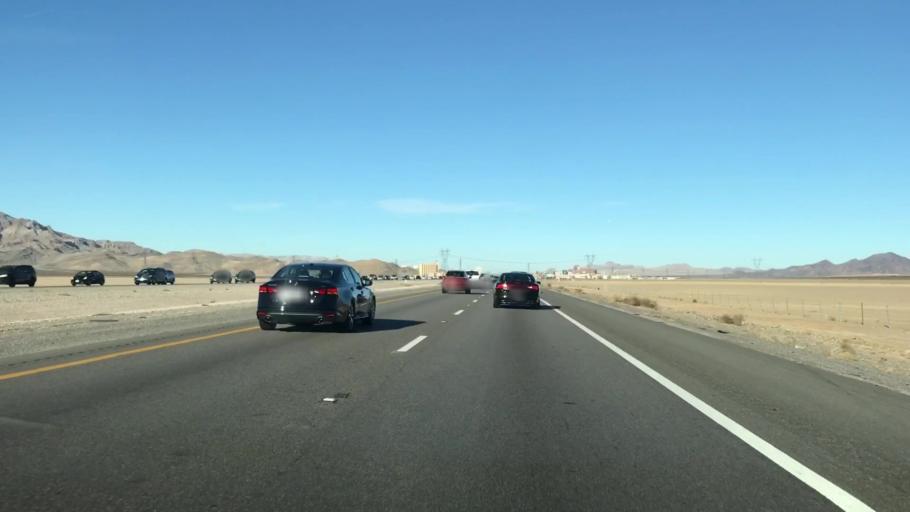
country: US
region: Nevada
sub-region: Clark County
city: Sandy Valley
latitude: 35.5824
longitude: -115.4015
